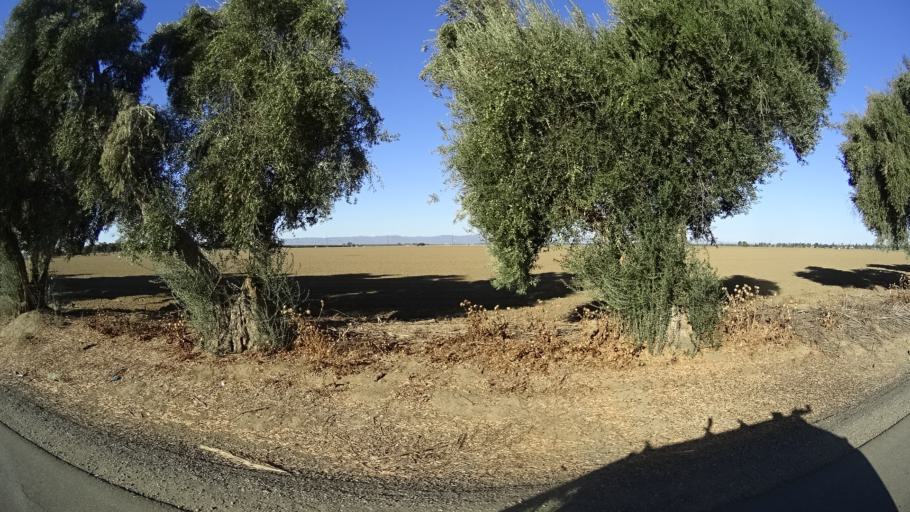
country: US
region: California
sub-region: Yolo County
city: Woodland
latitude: 38.6445
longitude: -121.7846
